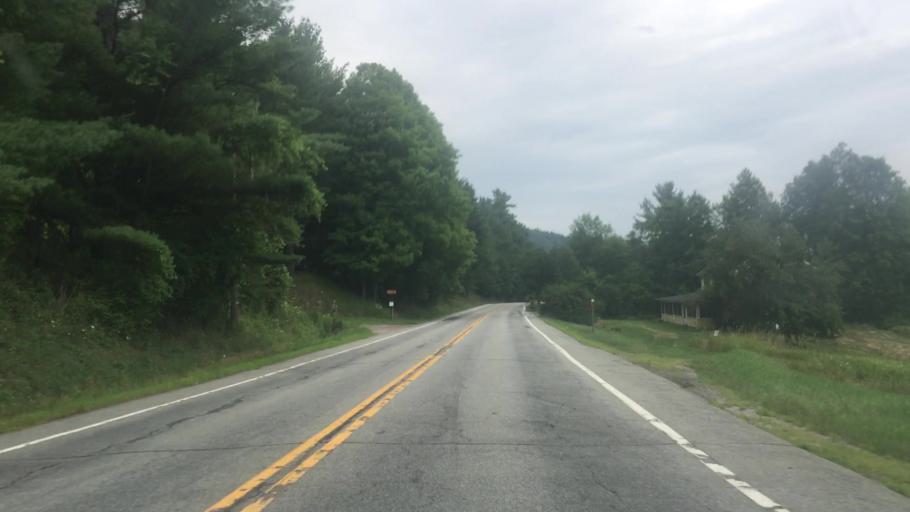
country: US
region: New York
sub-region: Essex County
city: Elizabethtown
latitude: 44.4016
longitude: -73.7061
